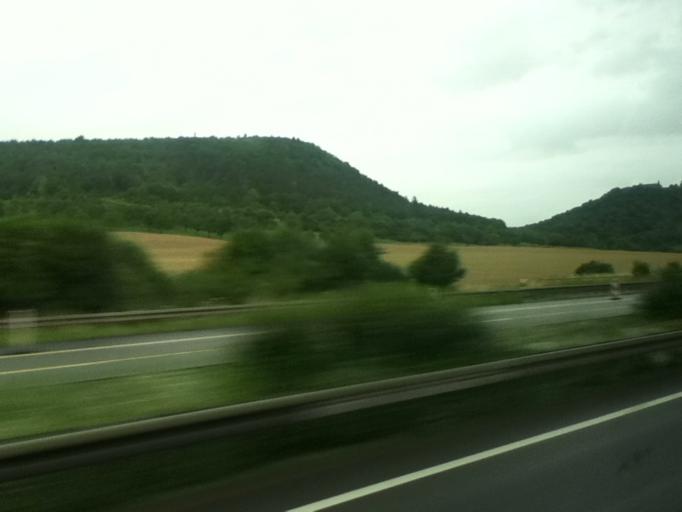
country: DE
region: Thuringia
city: Wandersleben
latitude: 50.8775
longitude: 10.8220
